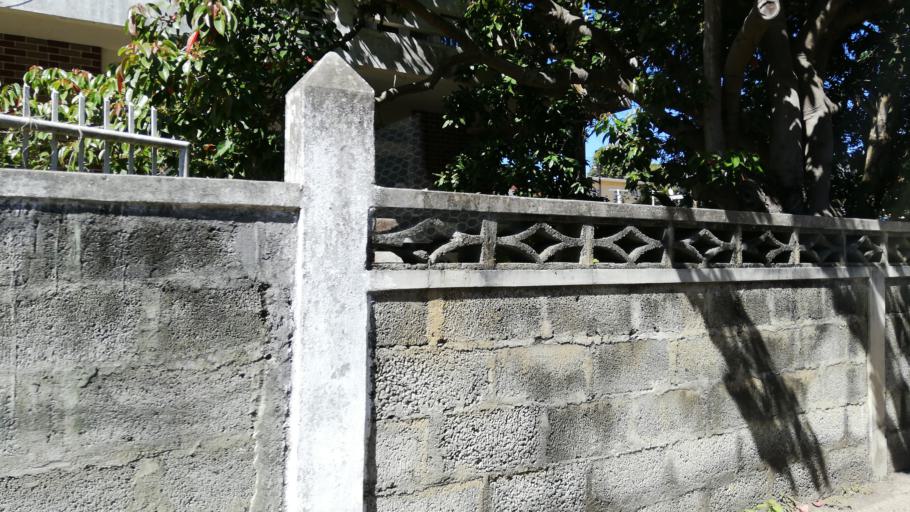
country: MU
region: Plaines Wilhems
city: Ebene
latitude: -20.2366
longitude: 57.4749
